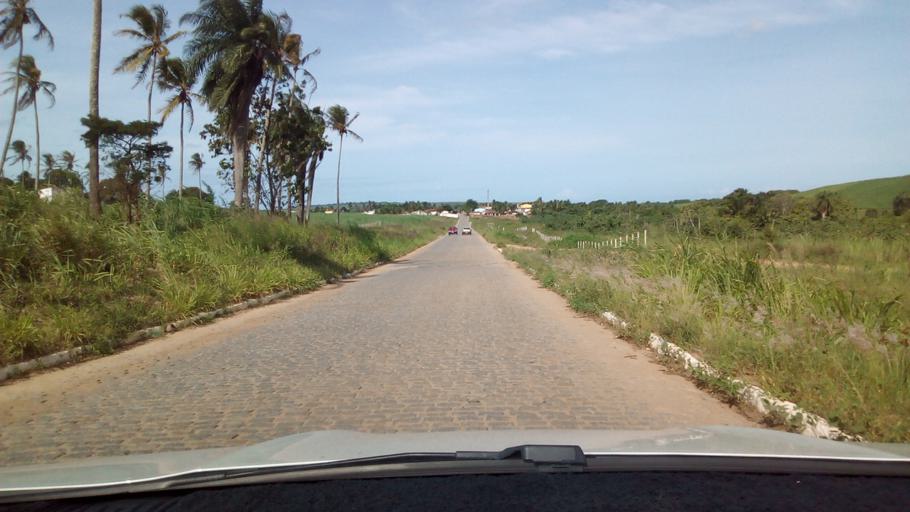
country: BR
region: Paraiba
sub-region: Santa Rita
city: Santa Rita
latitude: -7.0826
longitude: -34.9682
